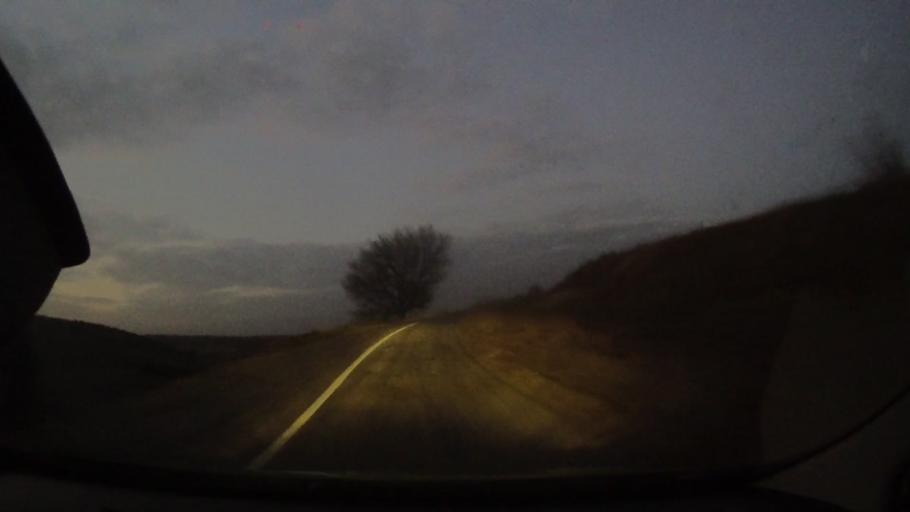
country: RO
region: Constanta
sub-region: Comuna Aliman
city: Aliman
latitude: 44.1487
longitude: 27.8331
